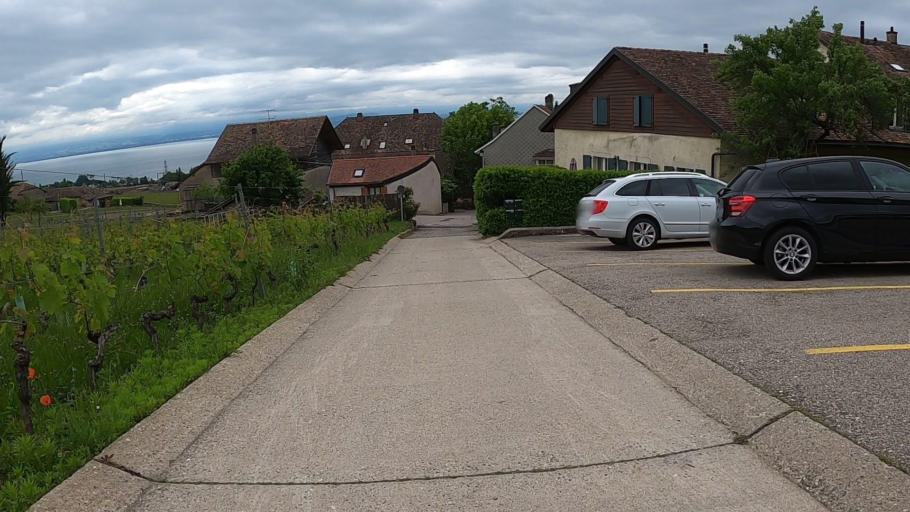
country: CH
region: Vaud
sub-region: Nyon District
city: Rolle
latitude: 46.4707
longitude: 6.3311
